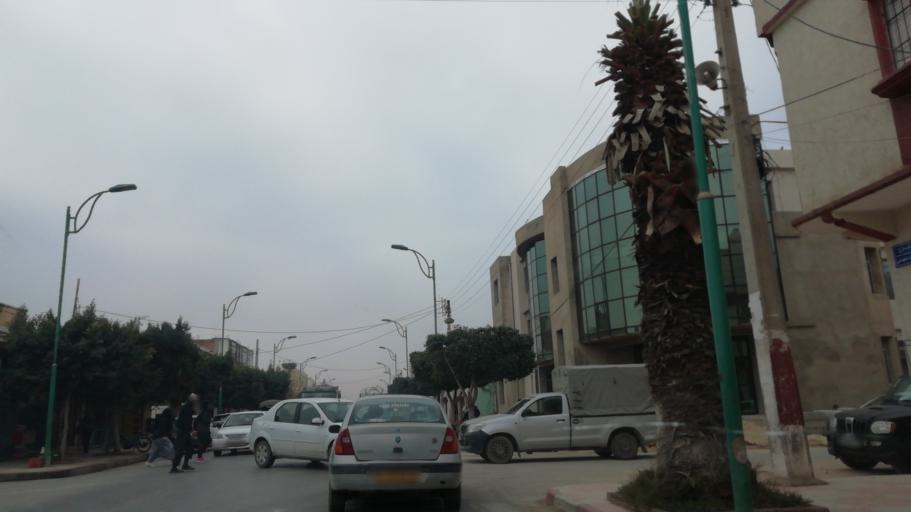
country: DZ
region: Relizane
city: Djidiouia
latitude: 35.9056
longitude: 0.7734
